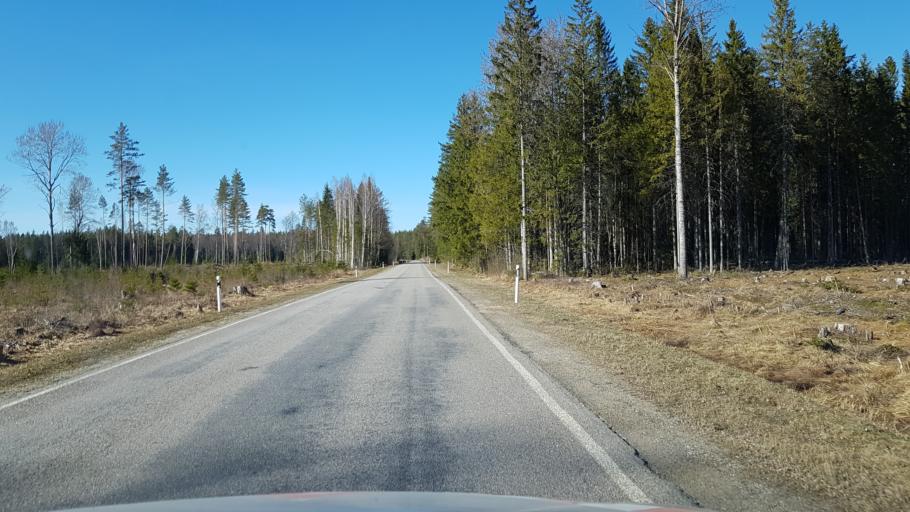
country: EE
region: Laeaene-Virumaa
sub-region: Vinni vald
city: Vinni
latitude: 59.2500
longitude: 26.6883
